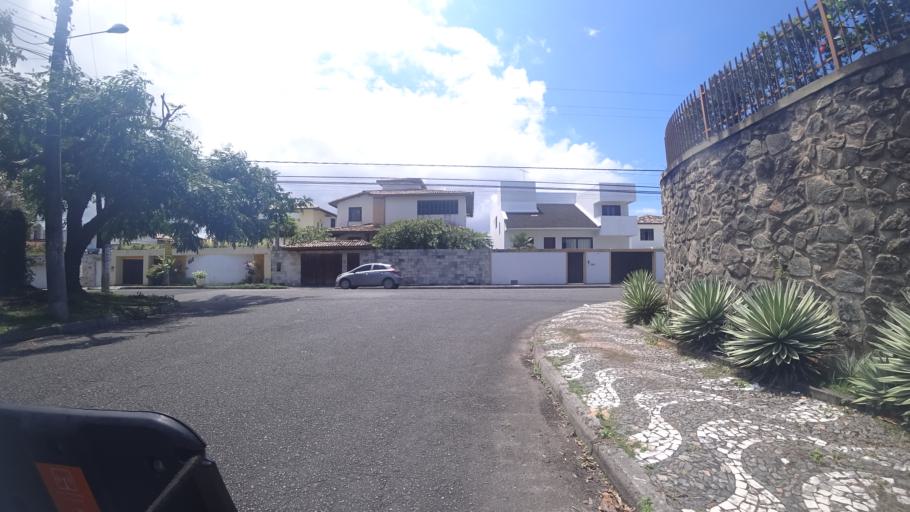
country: BR
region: Bahia
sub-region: Salvador
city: Salvador
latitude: -12.9925
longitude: -38.4698
